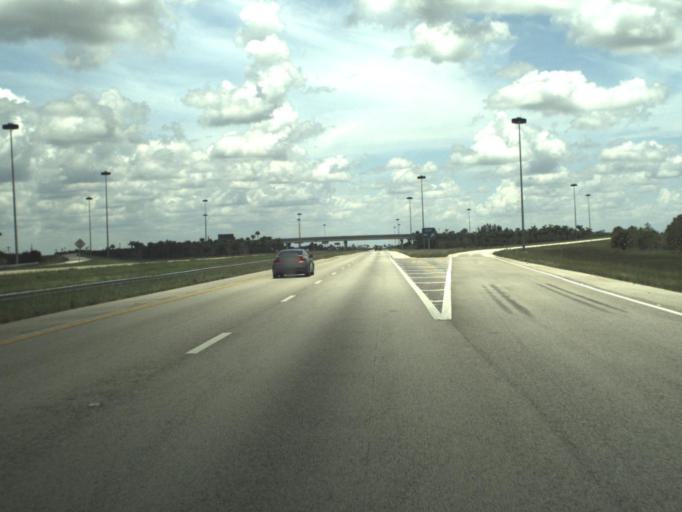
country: US
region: Florida
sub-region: Broward County
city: Weston
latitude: 26.1713
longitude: -80.8615
